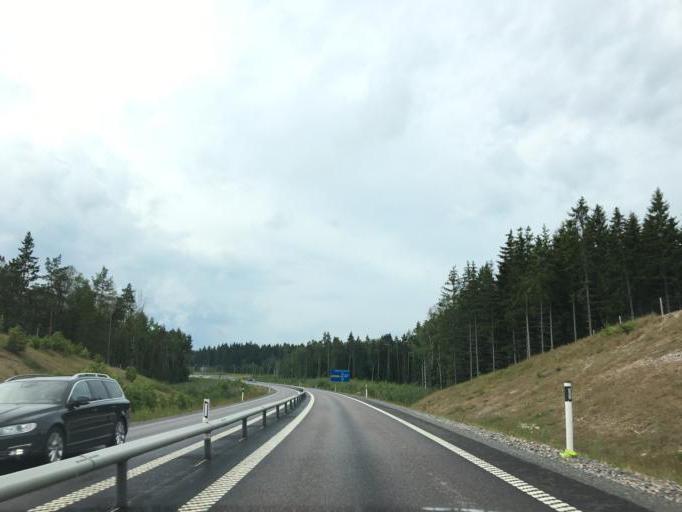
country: SE
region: Soedermanland
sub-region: Katrineholms Kommun
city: Katrineholm
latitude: 58.9358
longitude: 16.1994
